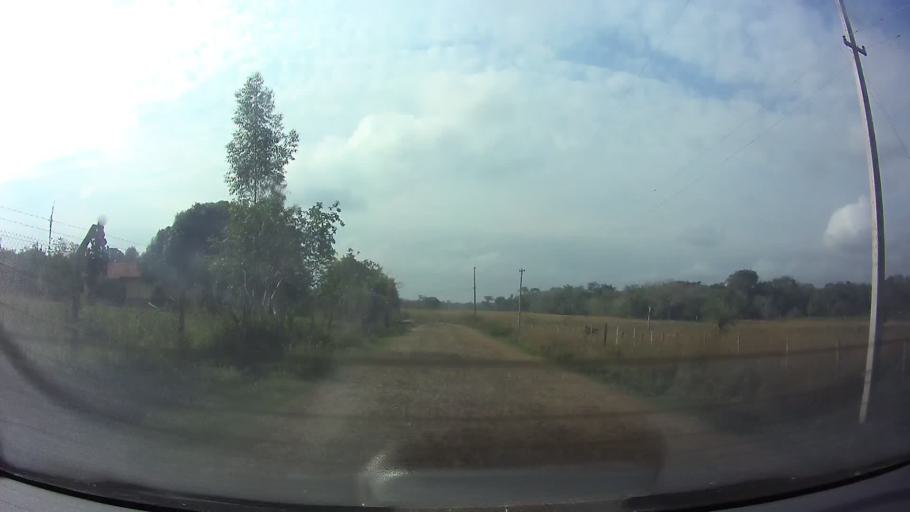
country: PY
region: Cordillera
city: Arroyos y Esteros
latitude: -25.0057
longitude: -57.1997
